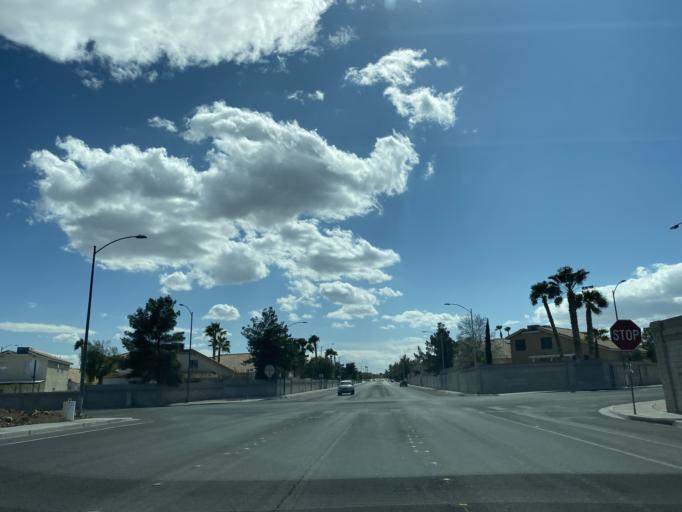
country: US
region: Nevada
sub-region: Clark County
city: Summerlin South
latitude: 36.2266
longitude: -115.2883
